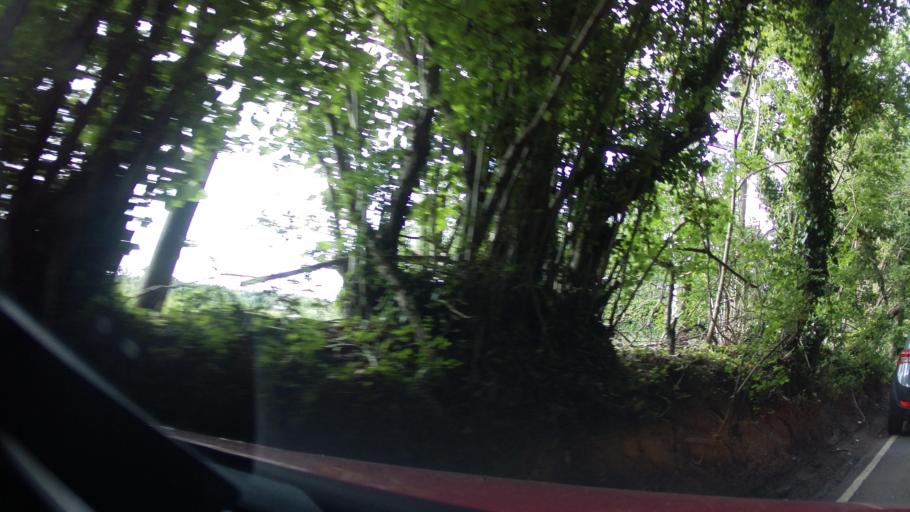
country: GB
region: England
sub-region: Hertfordshire
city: Chorleywood
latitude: 51.6698
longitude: -0.4628
